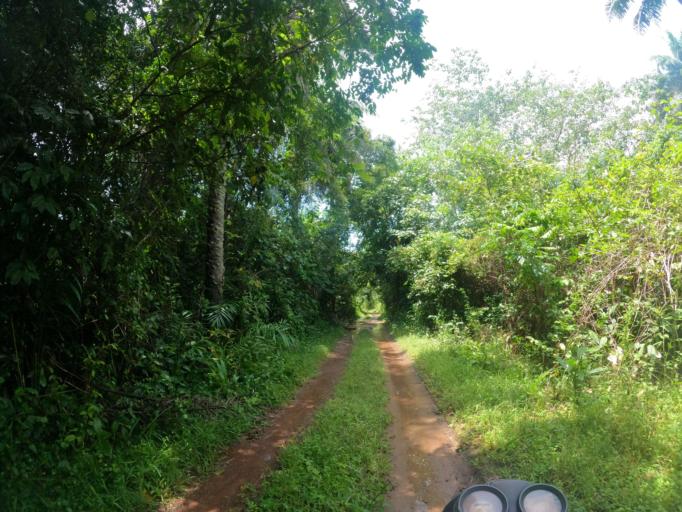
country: SL
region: Northern Province
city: Binkolo
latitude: 9.1567
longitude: -12.1926
